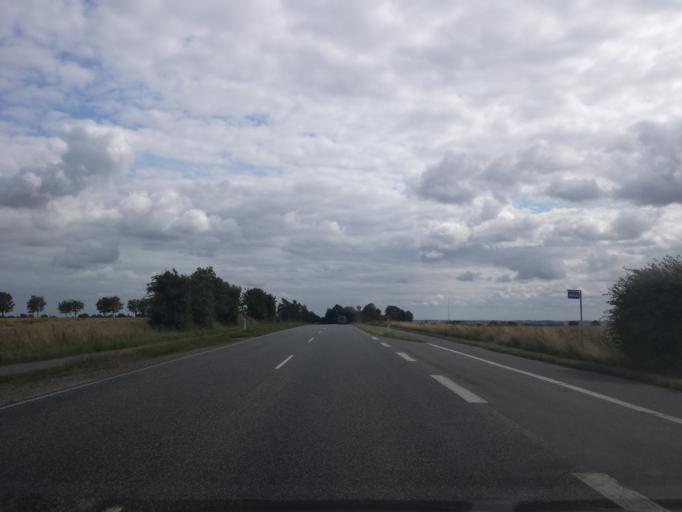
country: DK
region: South Denmark
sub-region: Sonderborg Kommune
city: Guderup
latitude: 55.0073
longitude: 9.8457
